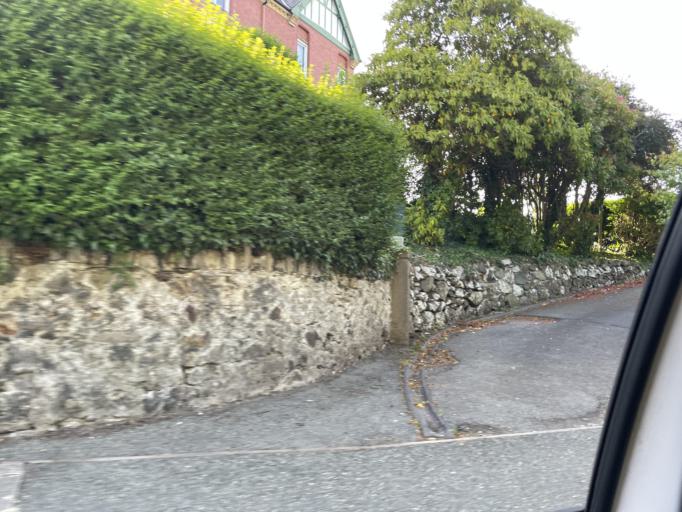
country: GB
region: Wales
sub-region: Gwynedd
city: Bangor
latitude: 53.2290
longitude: -4.1315
